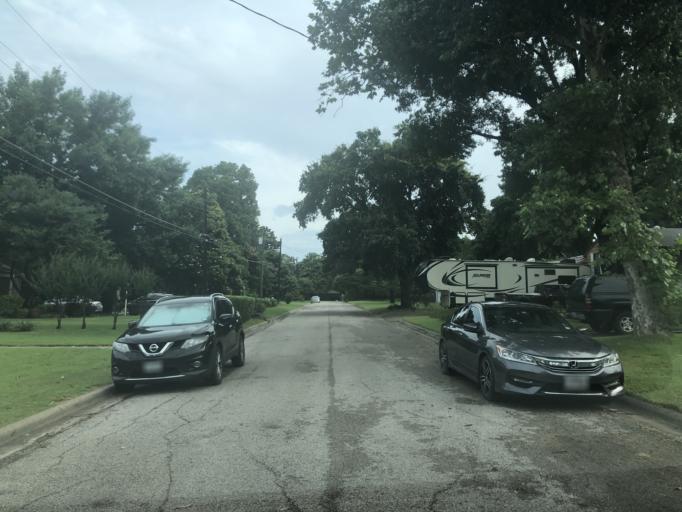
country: US
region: Texas
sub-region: Dallas County
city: Irving
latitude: 32.8047
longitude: -96.9450
